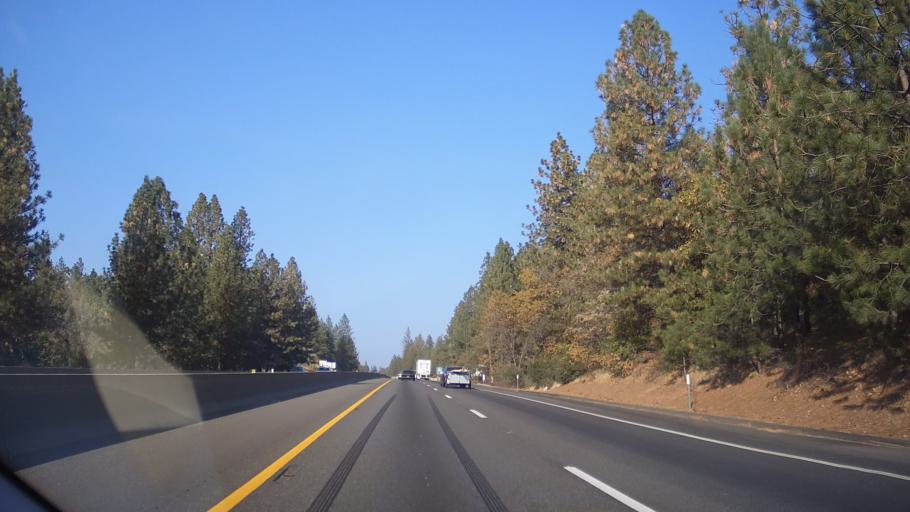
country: US
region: California
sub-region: Placer County
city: Meadow Vista
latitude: 39.0251
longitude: -120.9778
